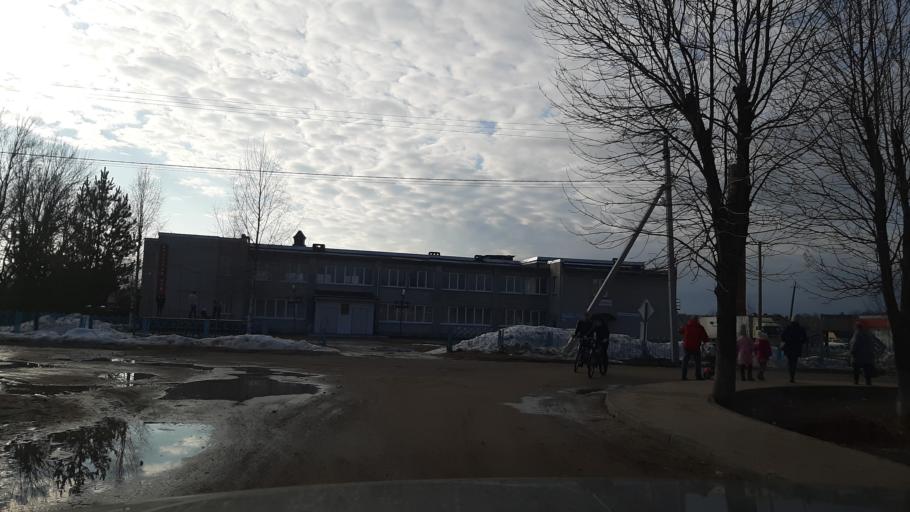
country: RU
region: Ivanovo
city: Novo-Talitsy
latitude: 56.9213
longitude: 40.7355
